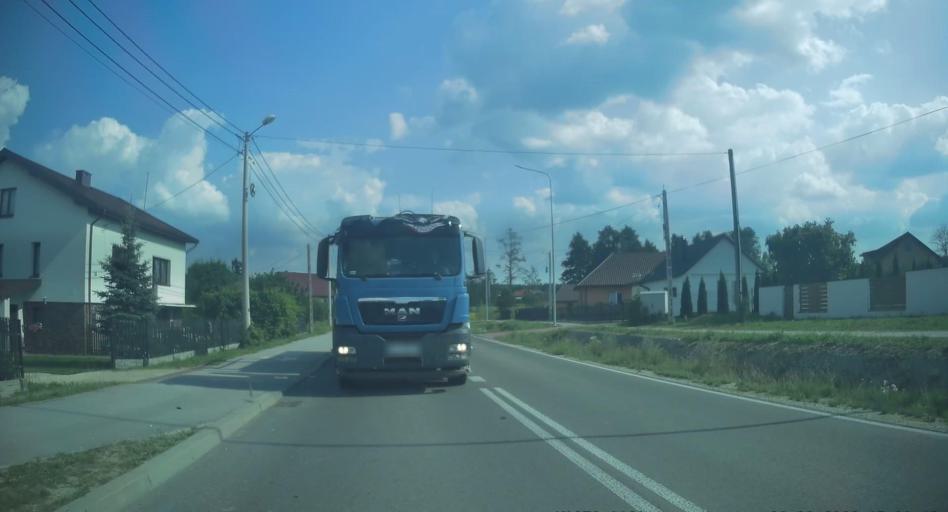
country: PL
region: Swietokrzyskie
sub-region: Powiat konecki
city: Radoszyce
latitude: 51.0320
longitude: 20.2884
